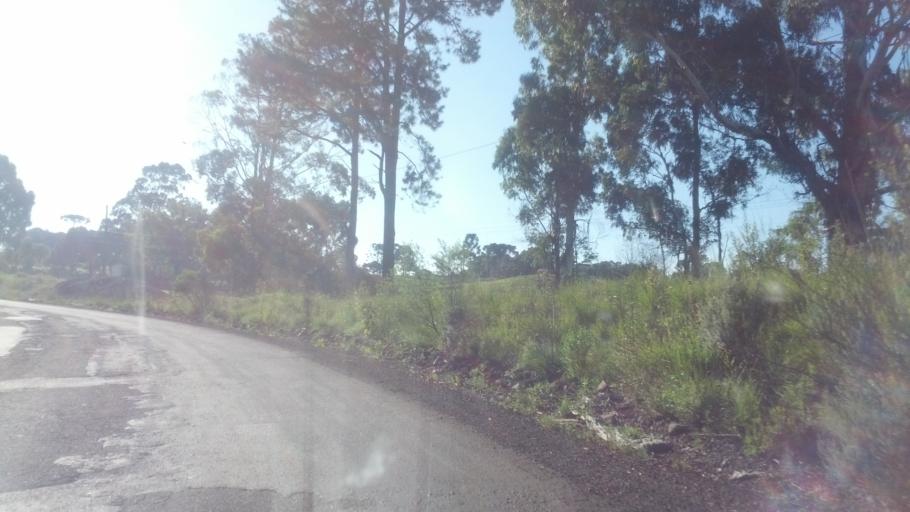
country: BR
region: Santa Catarina
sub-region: Lages
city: Lages
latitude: -27.9211
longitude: -50.5705
